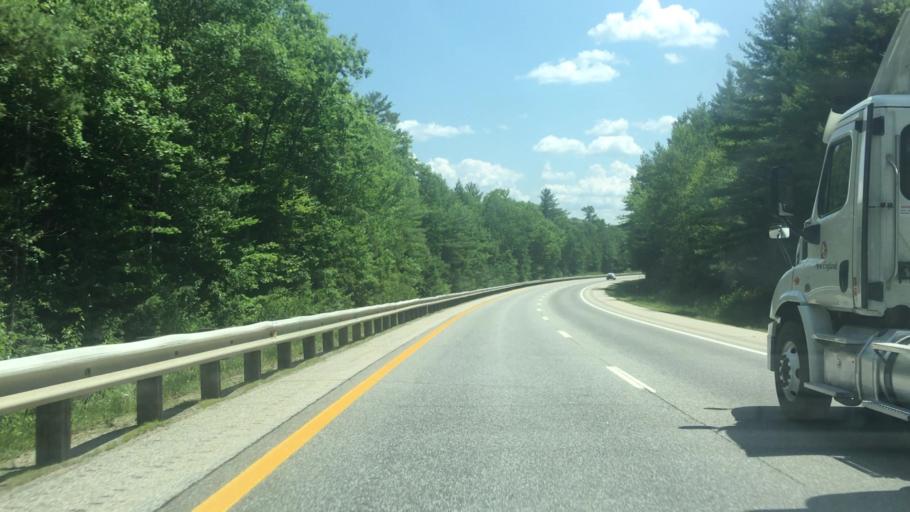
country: US
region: New Hampshire
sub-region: Merrimack County
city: Sutton
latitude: 43.3106
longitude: -71.8468
